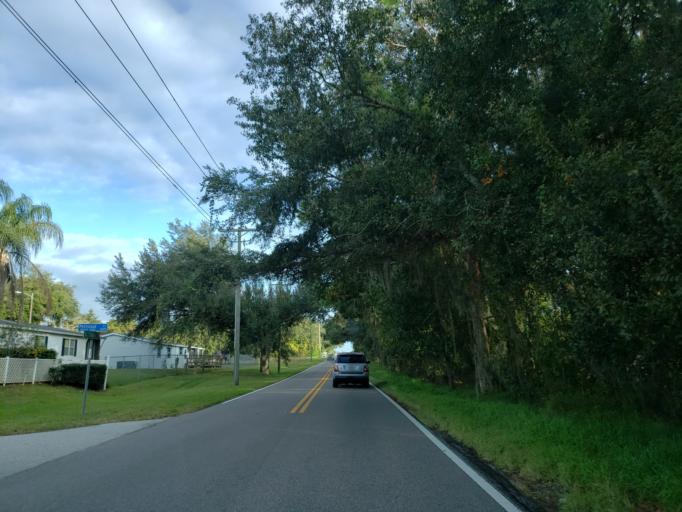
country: US
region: Florida
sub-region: Hillsborough County
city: Valrico
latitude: 27.9324
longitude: -82.2196
